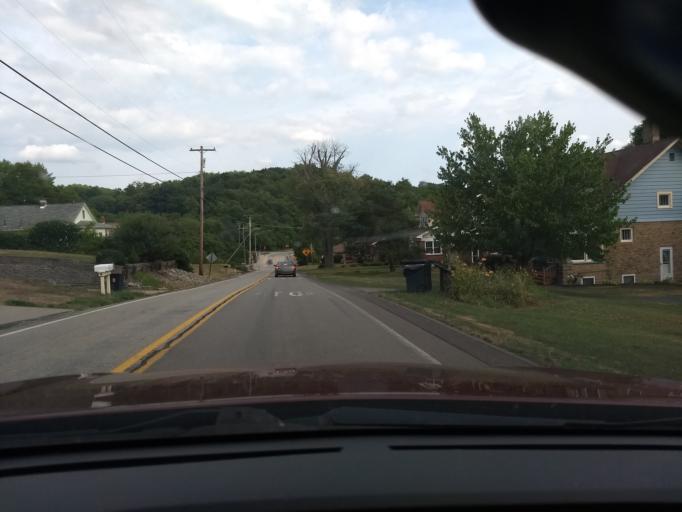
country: US
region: Pennsylvania
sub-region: Allegheny County
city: Curtisville
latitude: 40.6548
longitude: -79.8406
